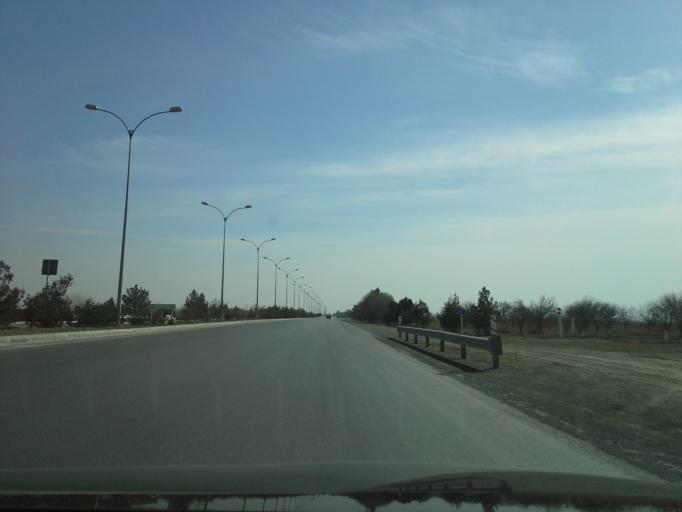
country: TM
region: Ahal
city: Abadan
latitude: 38.1235
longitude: 58.0368
